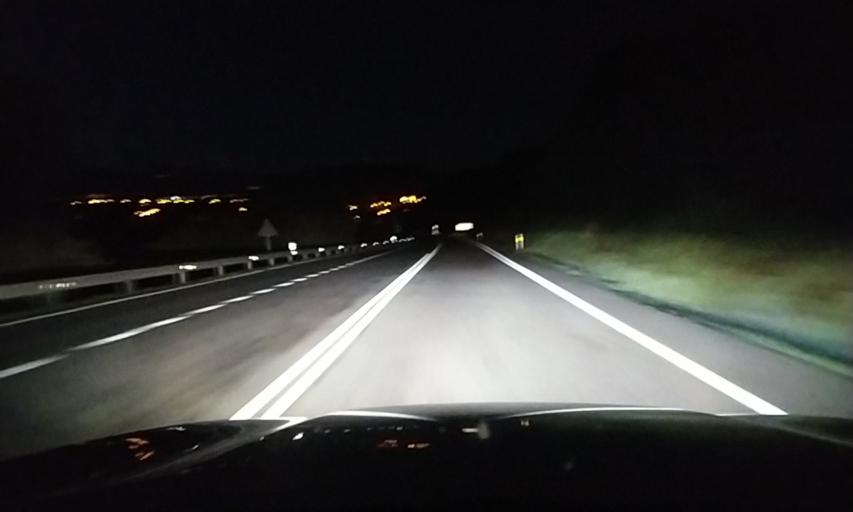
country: ES
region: Galicia
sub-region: Provincia de Ourense
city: Verin
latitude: 41.9570
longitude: -7.5014
